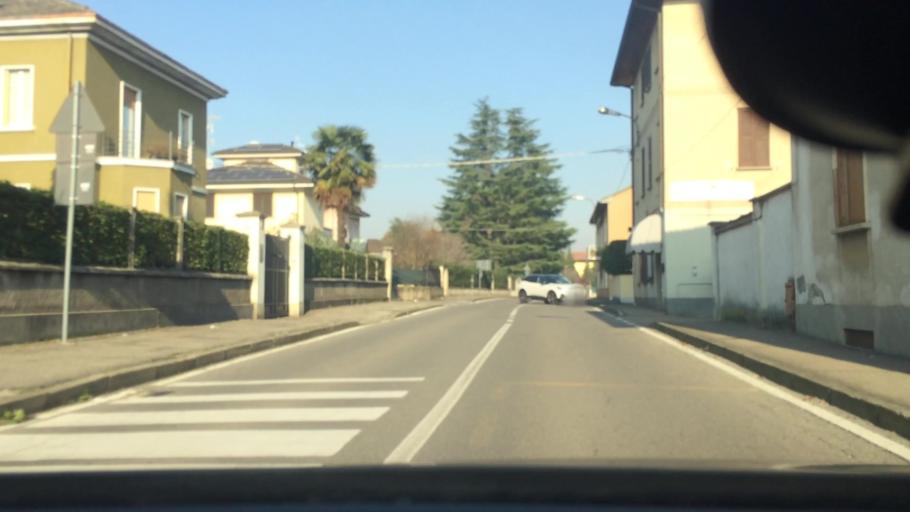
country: IT
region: Lombardy
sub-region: Provincia di Monza e Brianza
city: Misinto
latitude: 45.6652
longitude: 9.0832
